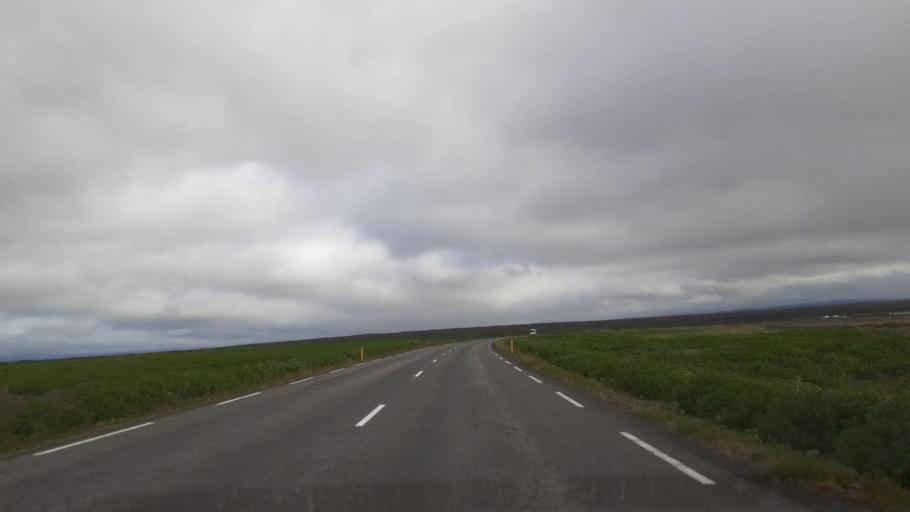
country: IS
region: Northeast
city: Husavik
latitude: 66.1140
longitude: -16.9081
